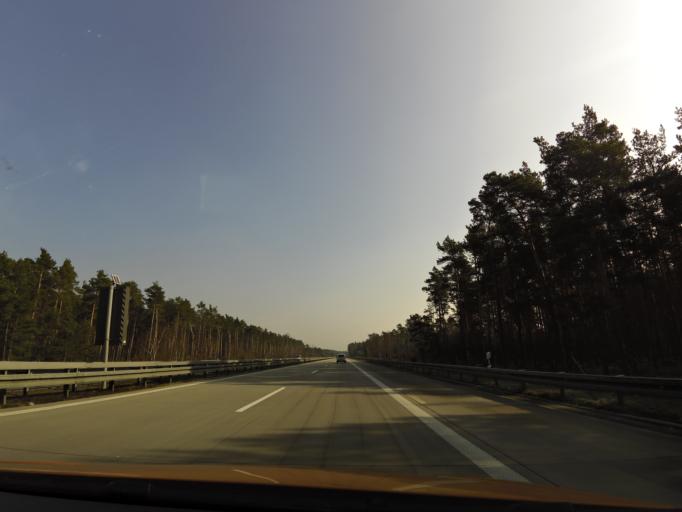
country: DE
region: Brandenburg
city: Briesen
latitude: 52.3363
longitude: 14.2305
